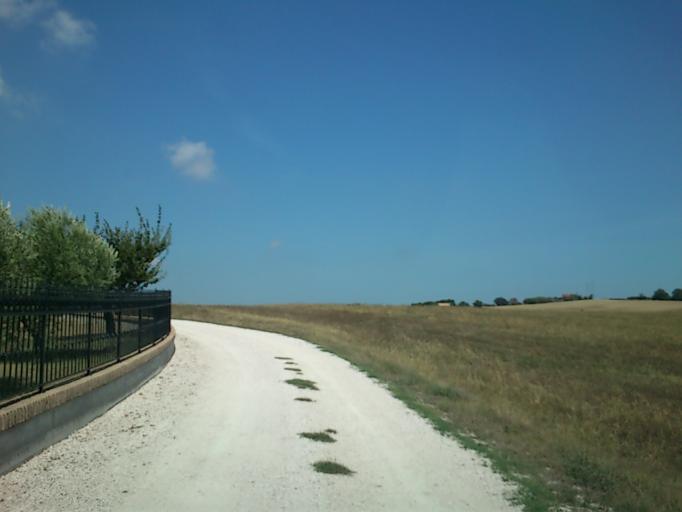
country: IT
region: The Marches
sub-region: Provincia di Pesaro e Urbino
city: Lucrezia
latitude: 43.7808
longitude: 12.9242
